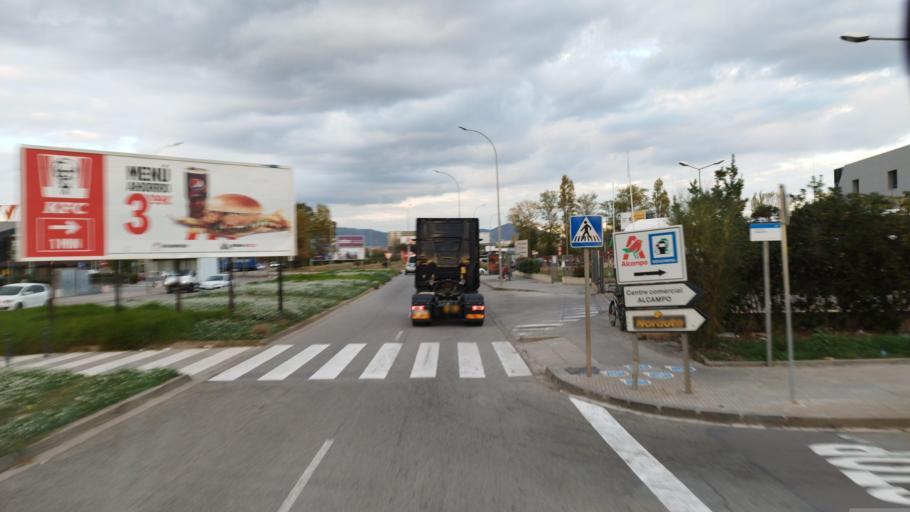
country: ES
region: Catalonia
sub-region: Provincia de Barcelona
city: Sant Boi de Llobregat
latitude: 41.3334
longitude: 2.0515
